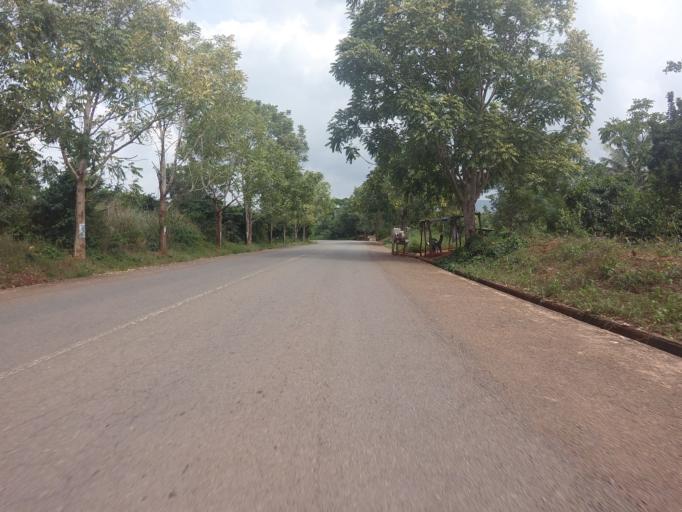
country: GH
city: Akropong
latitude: 5.9559
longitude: -0.1776
